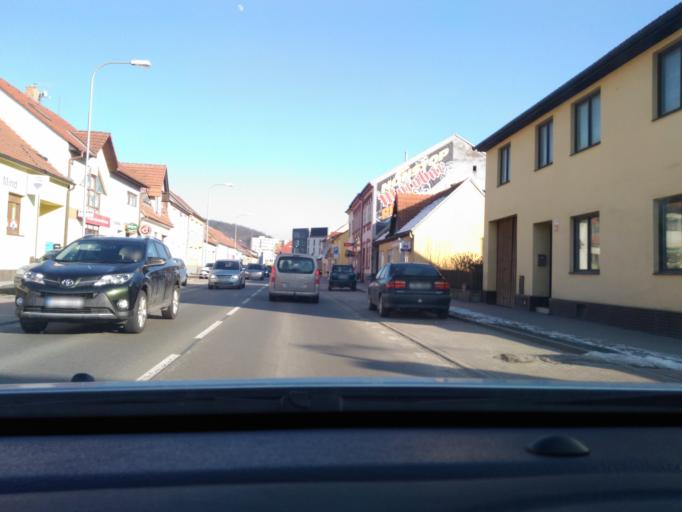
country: CZ
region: South Moravian
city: Kurim
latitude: 49.2981
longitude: 16.5346
